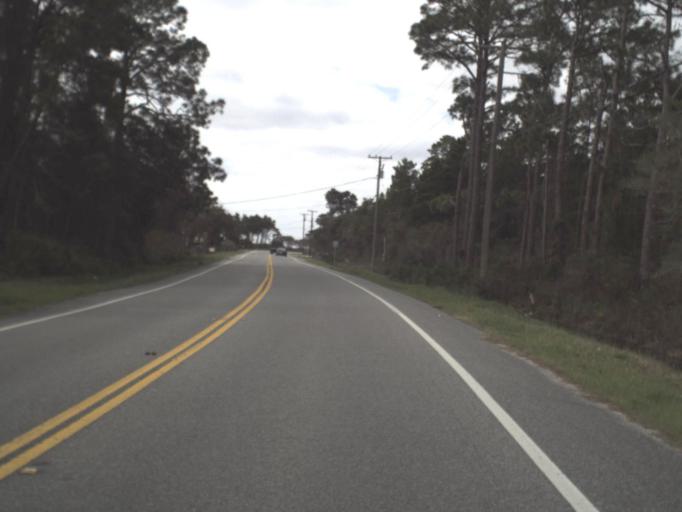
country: US
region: Florida
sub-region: Franklin County
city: Carrabelle
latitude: 29.8241
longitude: -84.7058
